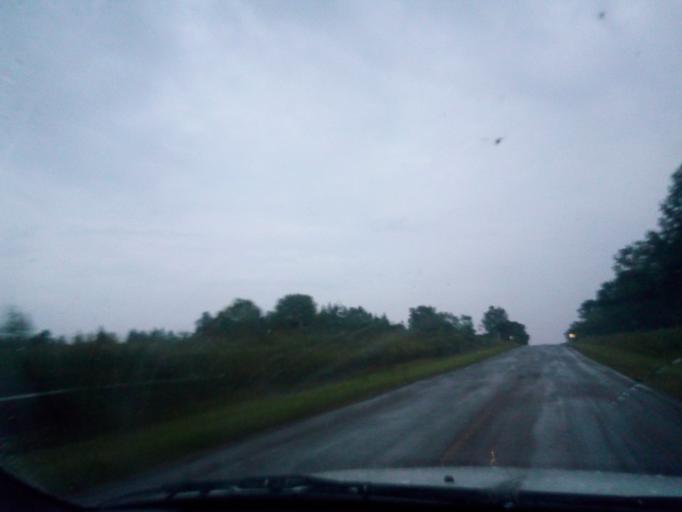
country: RU
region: Primorskiy
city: Lazo
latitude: 45.8701
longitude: 133.7087
